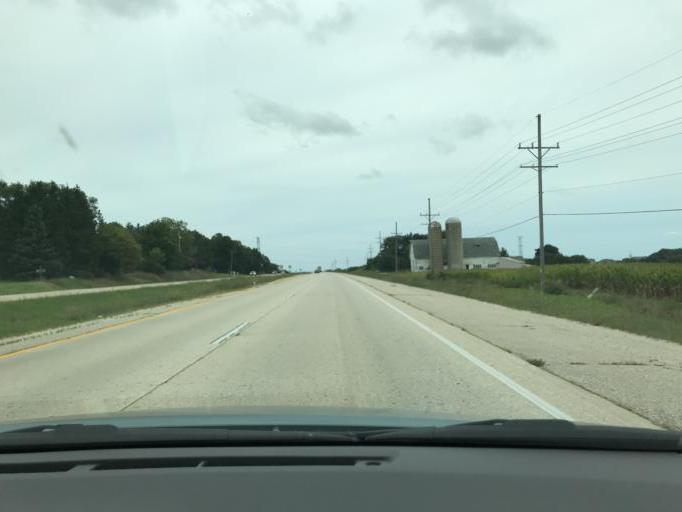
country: US
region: Wisconsin
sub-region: Kenosha County
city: Pleasant Prairie
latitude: 42.5672
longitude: -87.9752
